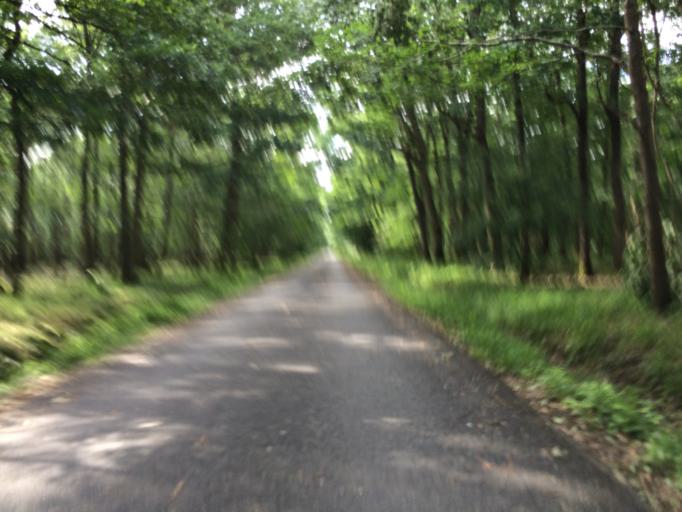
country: FR
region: Ile-de-France
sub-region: Departement de l'Essonne
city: Etiolles
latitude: 48.6571
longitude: 2.4778
